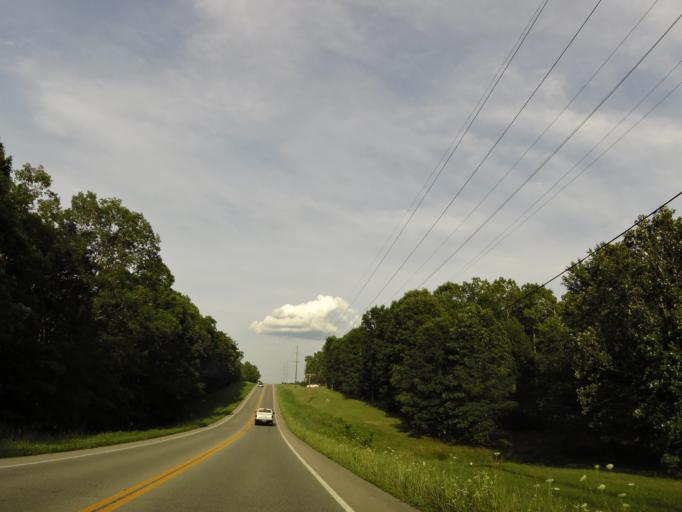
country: US
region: Tennessee
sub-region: Dickson County
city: Dickson
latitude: 36.0907
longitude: -87.5044
